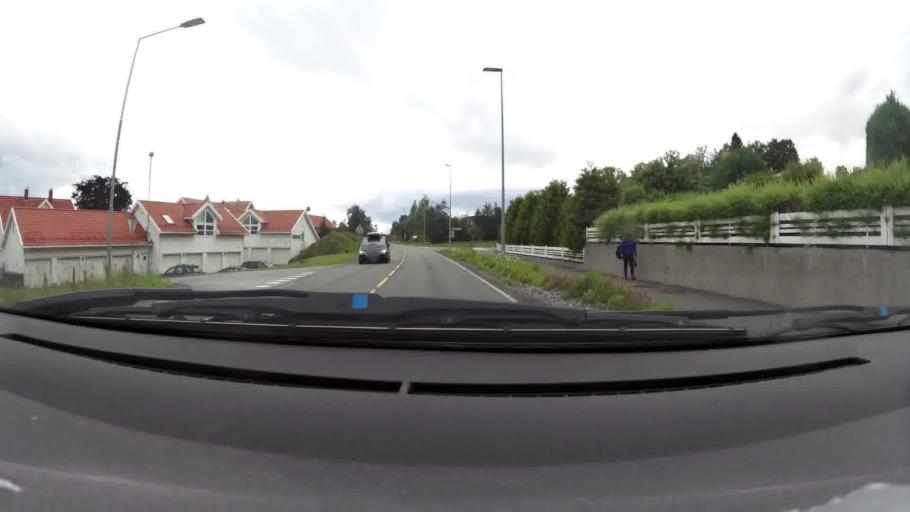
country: NO
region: More og Romsdal
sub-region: Molde
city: Molde
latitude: 62.7438
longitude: 7.1967
